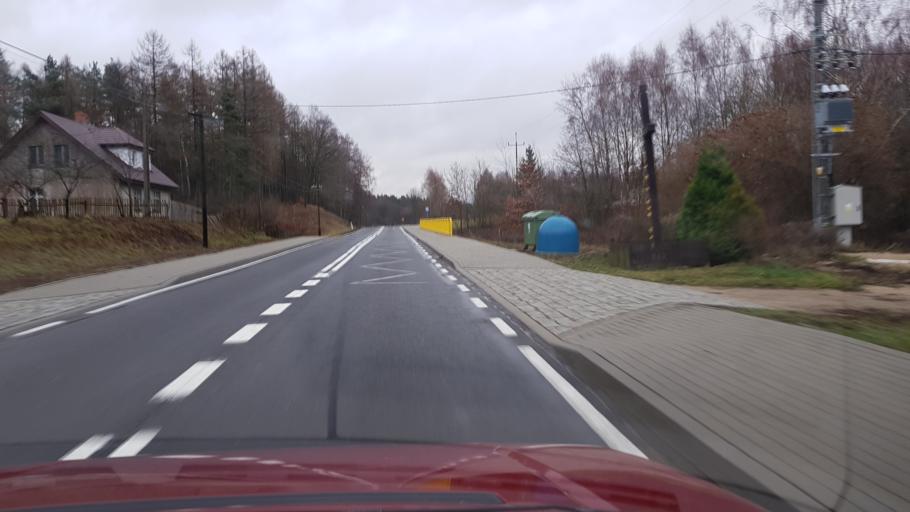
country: PL
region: West Pomeranian Voivodeship
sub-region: Powiat lobeski
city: Wegorzyno
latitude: 53.5205
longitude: 15.6273
